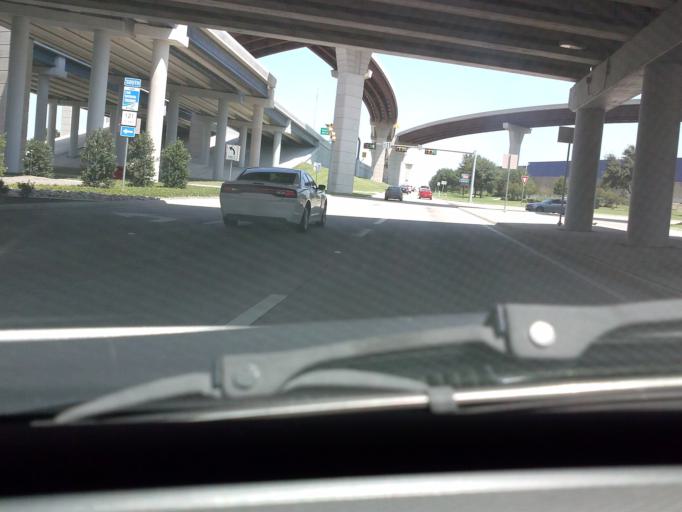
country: US
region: Texas
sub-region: Collin County
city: Frisco
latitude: 33.0912
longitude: -96.8224
